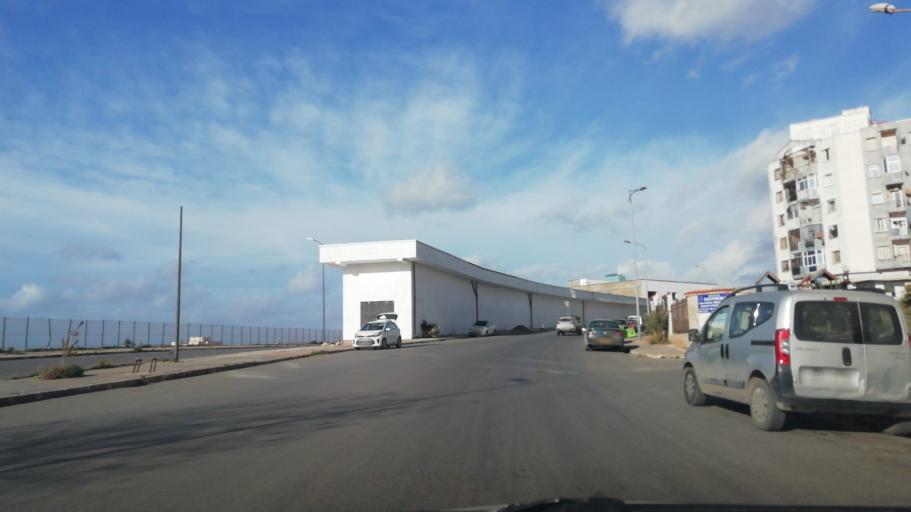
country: DZ
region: Oran
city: Bir el Djir
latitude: 35.7210
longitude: -0.5957
